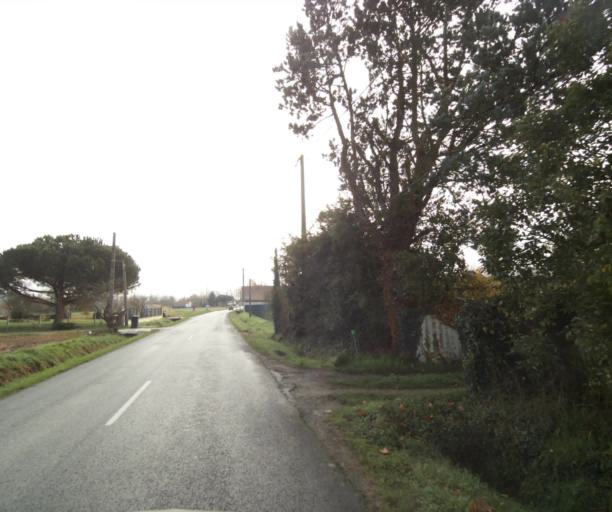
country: FR
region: Midi-Pyrenees
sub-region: Departement de la Haute-Garonne
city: Villemur-sur-Tarn
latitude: 43.8753
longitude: 1.4890
